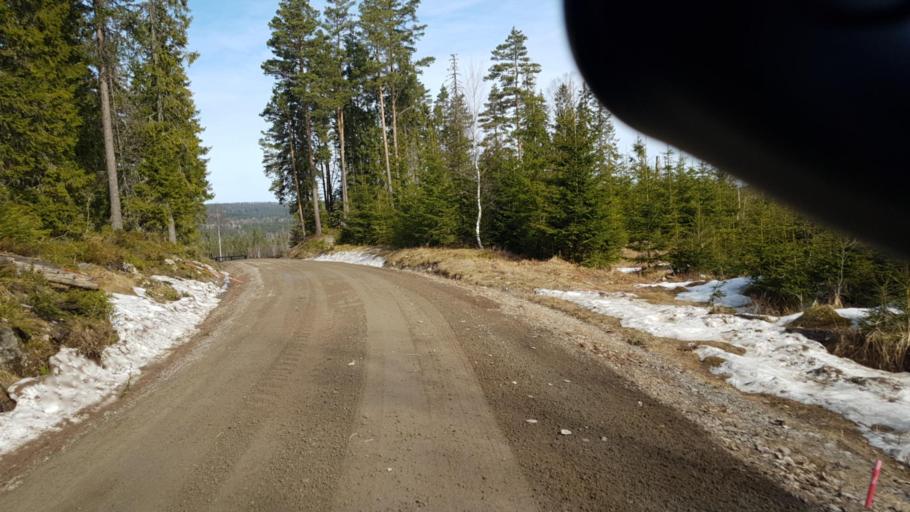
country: SE
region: Vaermland
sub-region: Arvika Kommun
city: Arvika
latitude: 59.5404
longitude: 12.4431
